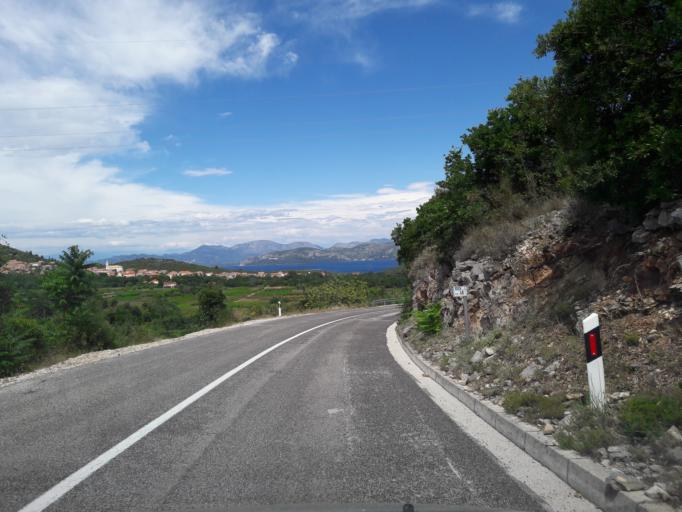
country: HR
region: Dubrovacko-Neretvanska
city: Blato
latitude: 42.9147
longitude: 17.4258
